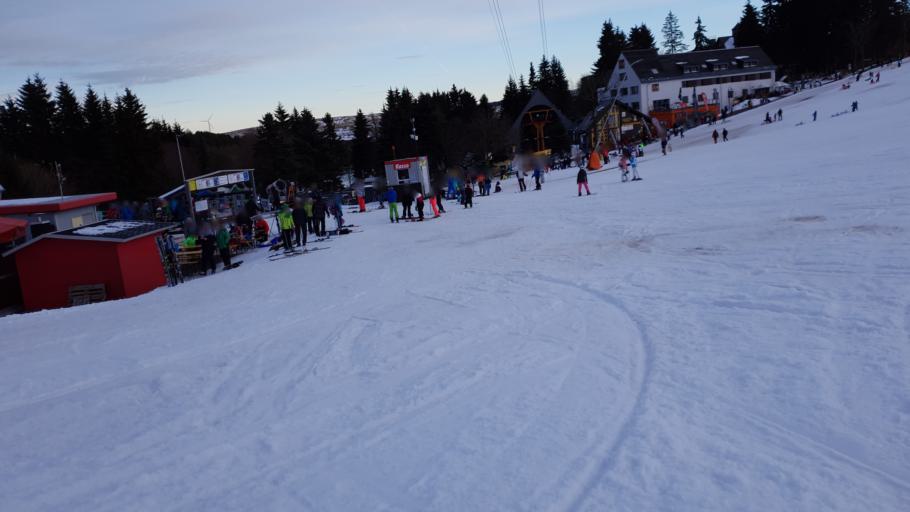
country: DE
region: Saxony
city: Kurort Oberwiesenthal
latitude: 50.4243
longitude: 12.9660
